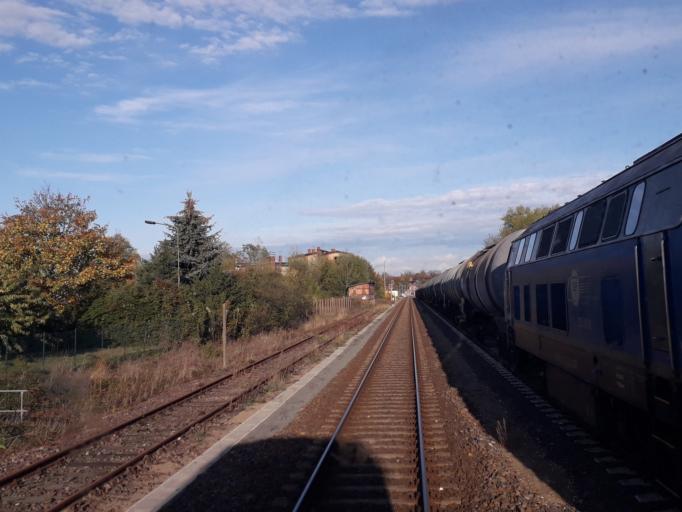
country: DE
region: Brandenburg
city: Perleberg
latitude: 53.0686
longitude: 11.8451
